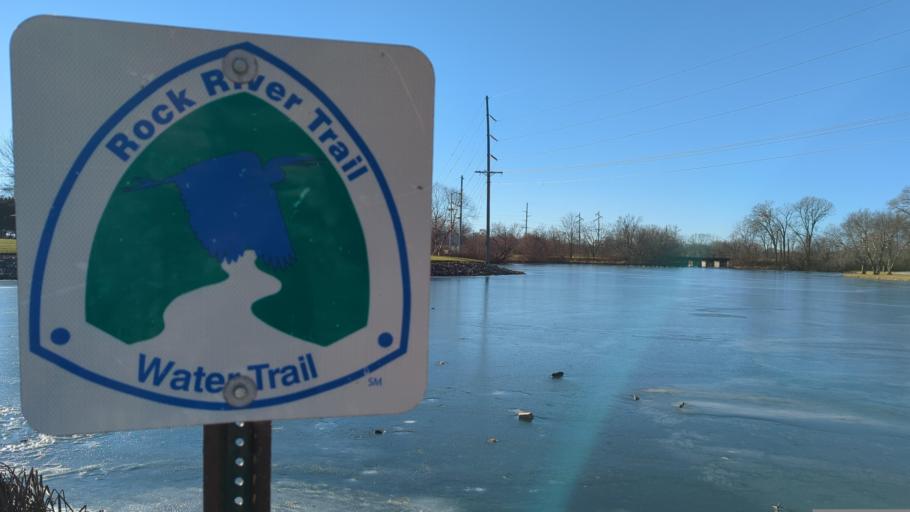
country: US
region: Wisconsin
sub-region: Fond du Lac County
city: Waupun
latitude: 43.6376
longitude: -88.7311
